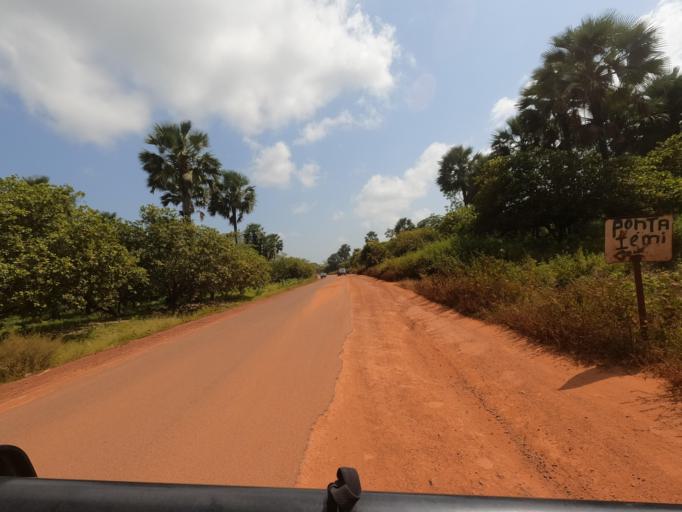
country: GW
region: Oio
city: Bissora
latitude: 12.2875
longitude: -15.7754
